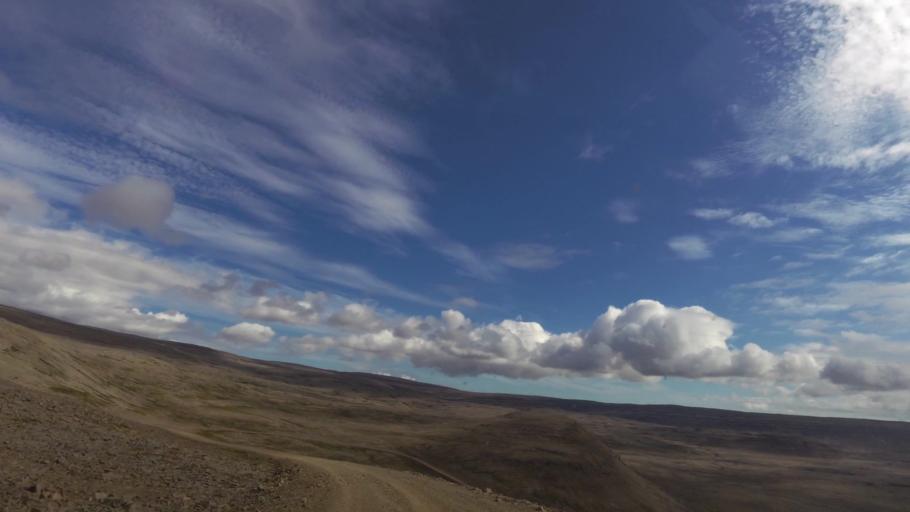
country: IS
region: West
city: Olafsvik
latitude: 65.6190
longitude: -24.3153
